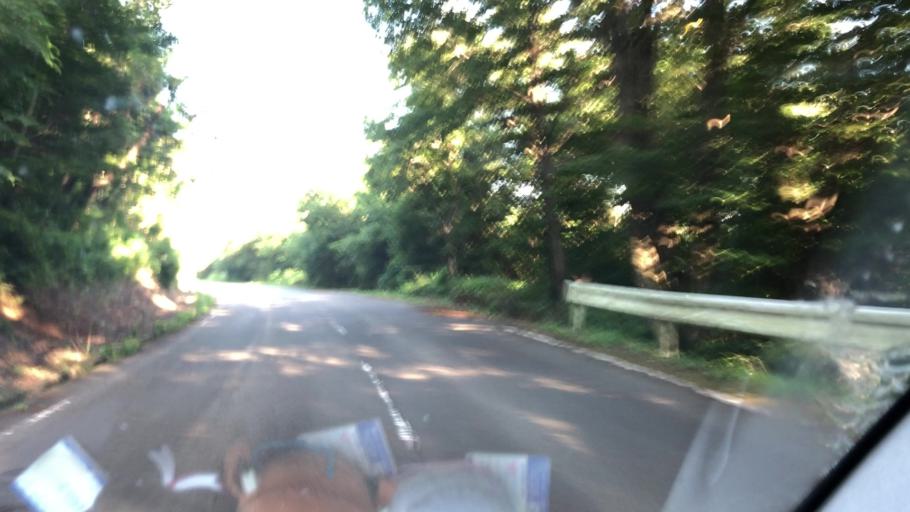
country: JP
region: Miyagi
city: Shiroishi
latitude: 38.0388
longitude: 140.5329
